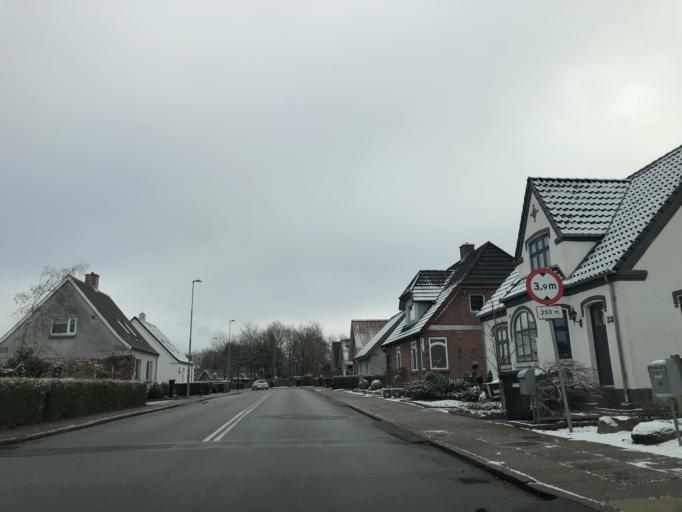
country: DK
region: South Denmark
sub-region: Vejle Kommune
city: Give
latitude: 55.9832
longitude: 9.2945
